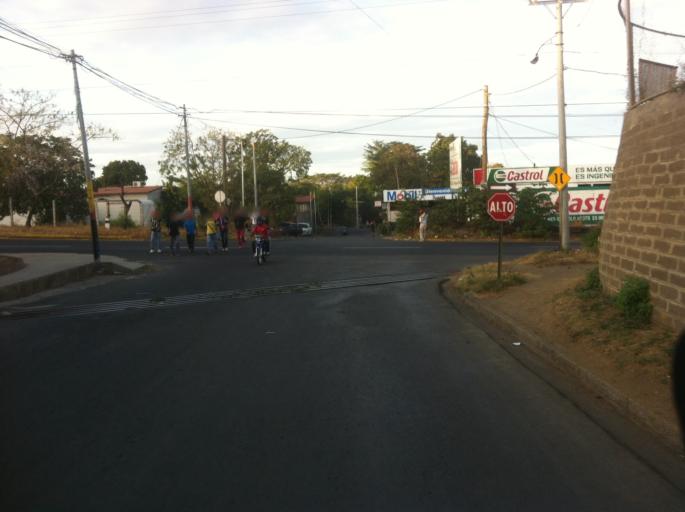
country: NI
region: Managua
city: Managua
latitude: 12.1061
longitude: -86.3002
